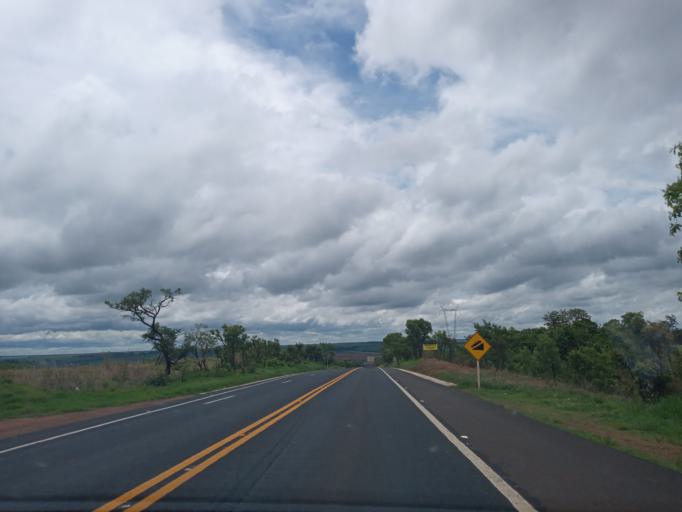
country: BR
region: Minas Gerais
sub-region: Uberaba
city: Uberaba
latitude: -19.2894
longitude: -47.6084
